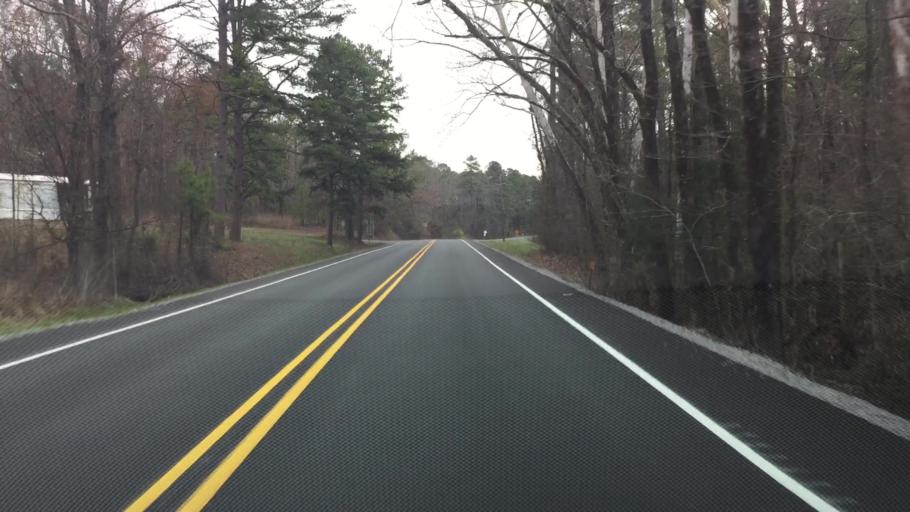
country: US
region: Arkansas
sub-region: Saline County
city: Haskell
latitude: 34.6151
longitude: -92.7896
